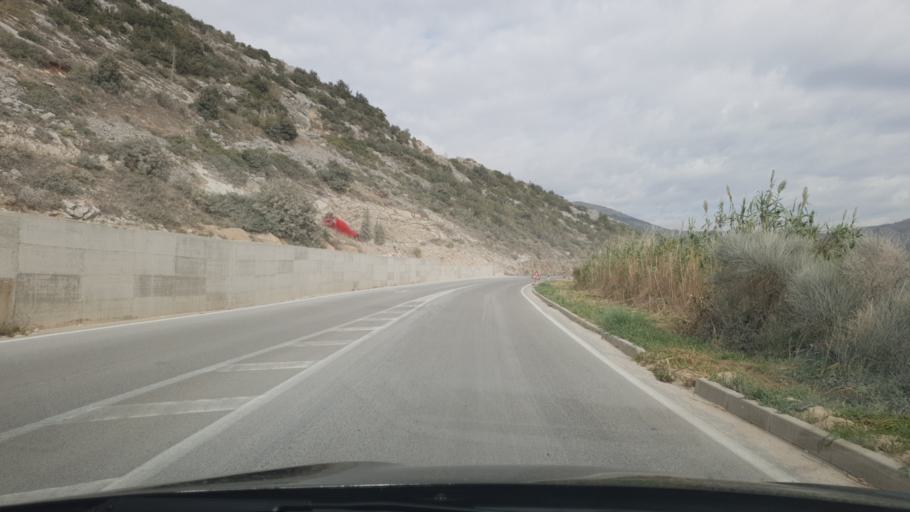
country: HR
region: Dubrovacko-Neretvanska
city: Cibaca
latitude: 42.6327
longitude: 18.1591
